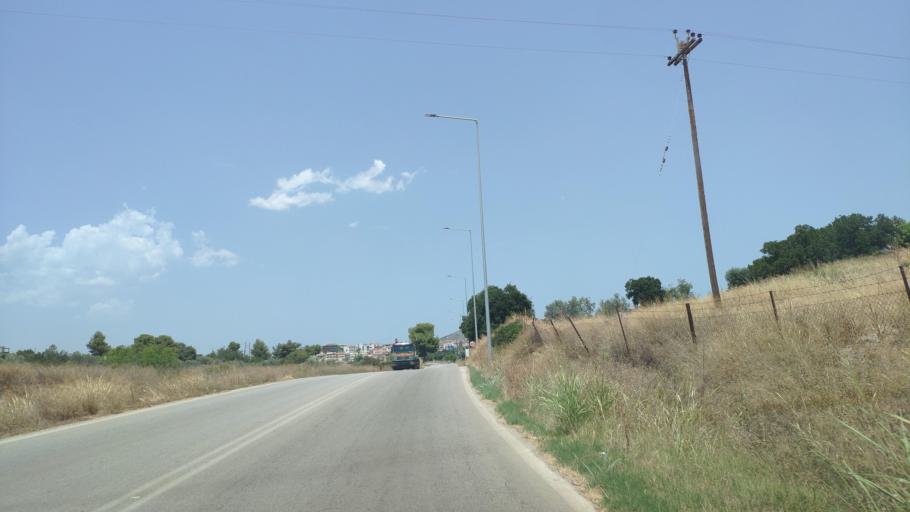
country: GR
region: Peloponnese
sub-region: Nomos Argolidos
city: Kranidi
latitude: 37.3672
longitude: 23.1621
